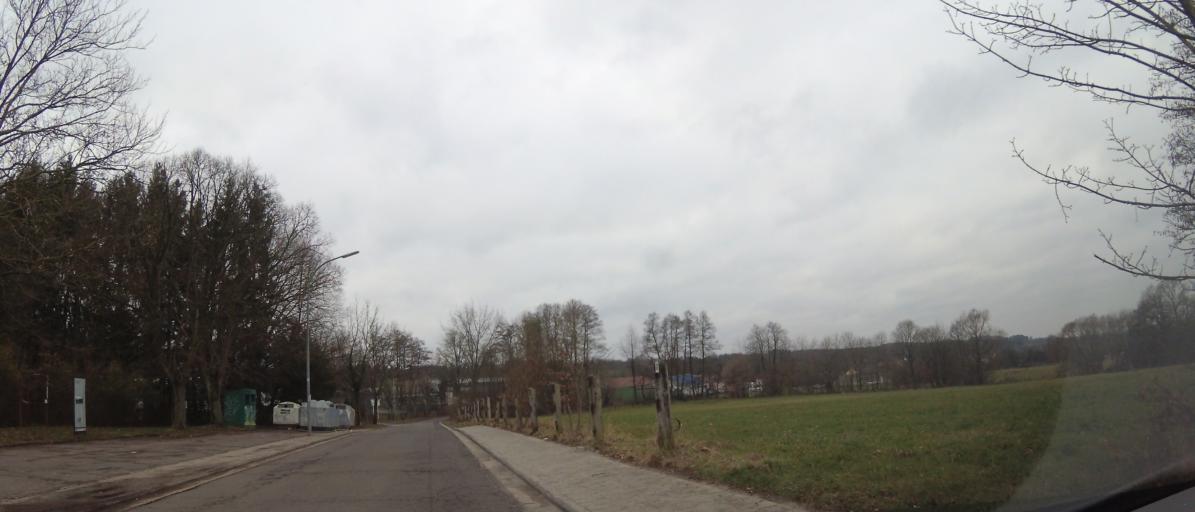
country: DE
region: Saarland
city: Mainzweiler
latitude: 49.3997
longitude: 7.1015
